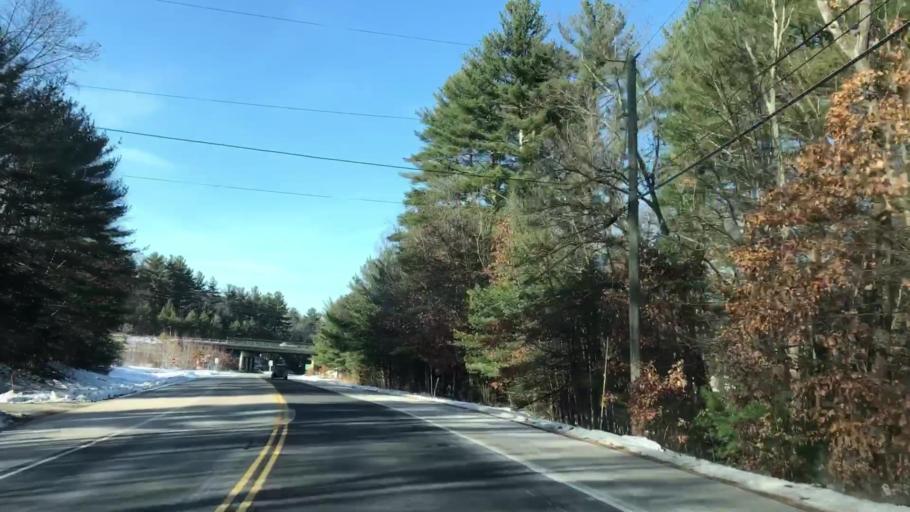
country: US
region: New Hampshire
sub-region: Hillsborough County
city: Milford
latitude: 42.8435
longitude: -71.6140
